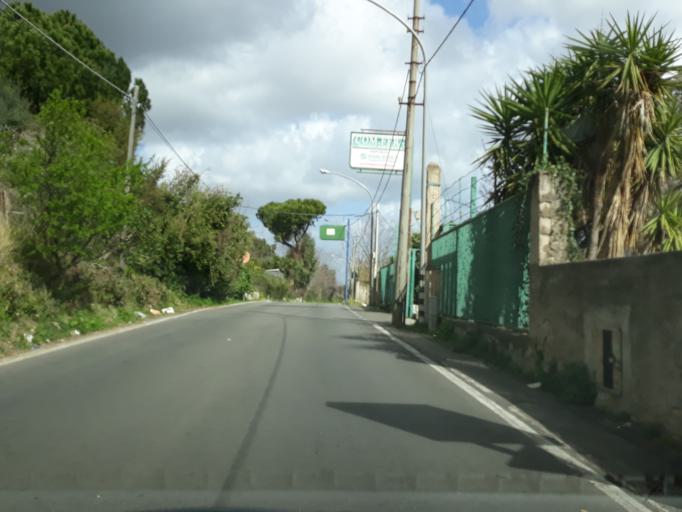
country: IT
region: Sicily
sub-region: Palermo
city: Monreale
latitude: 38.0987
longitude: 13.3099
